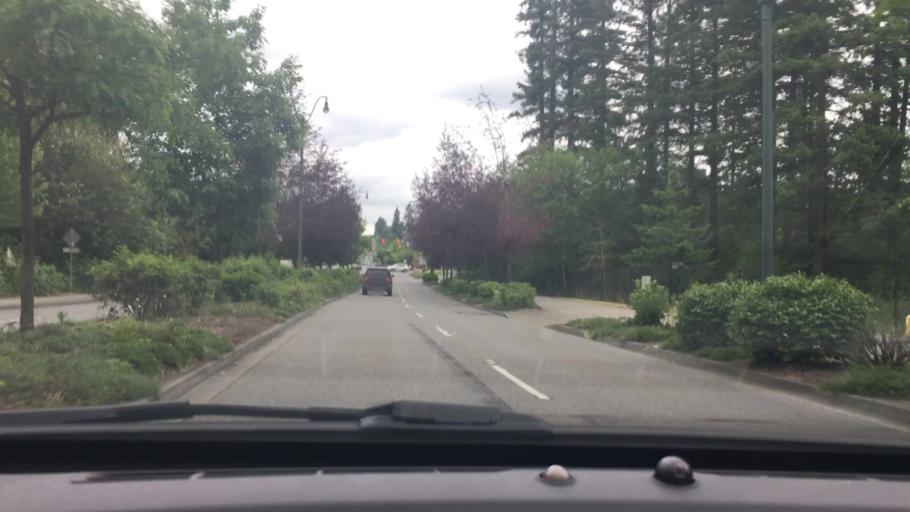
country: US
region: Washington
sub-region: King County
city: City of Sammamish
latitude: 47.6113
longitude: -122.0354
